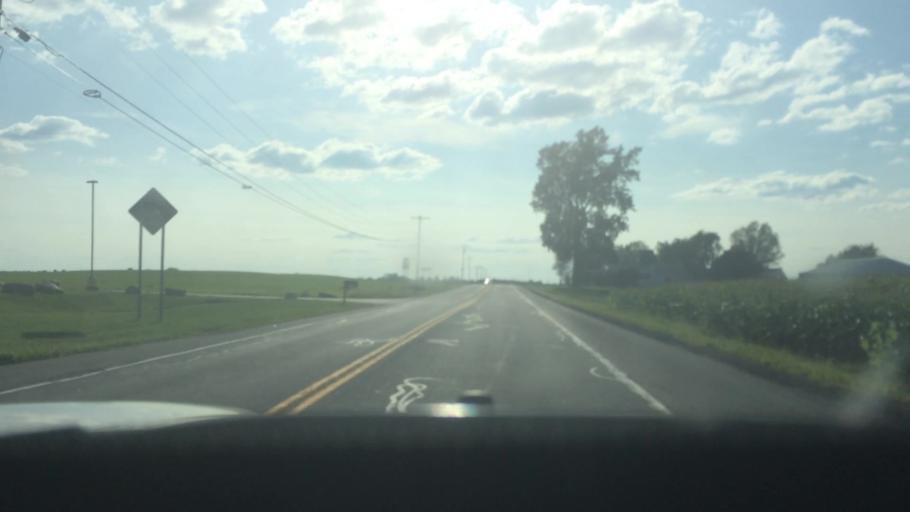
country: US
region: New York
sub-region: St. Lawrence County
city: Potsdam
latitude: 44.6895
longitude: -74.7097
